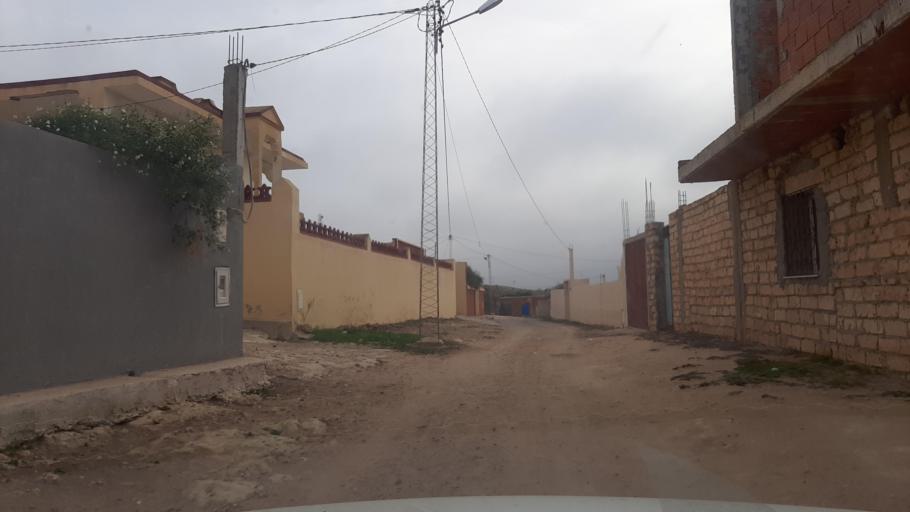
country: TN
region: Nabul
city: Menzel Heurr
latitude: 36.6635
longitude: 10.9122
